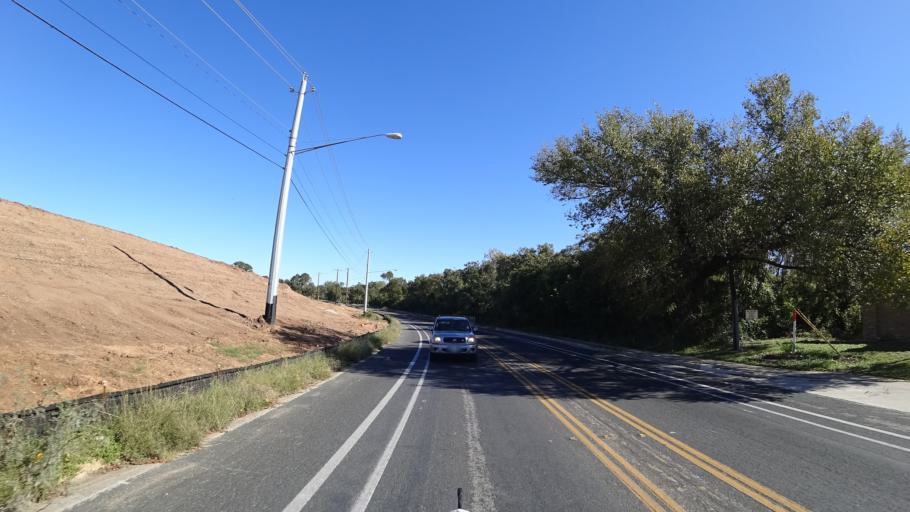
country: US
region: Texas
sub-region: Travis County
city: Austin
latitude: 30.2906
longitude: -97.6897
